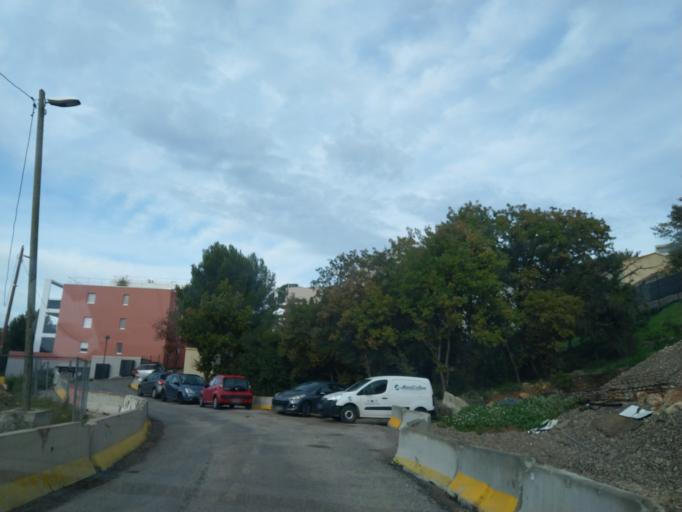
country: FR
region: Provence-Alpes-Cote d'Azur
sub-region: Departement des Bouches-du-Rhone
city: Marseille 12
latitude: 43.2987
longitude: 5.4436
